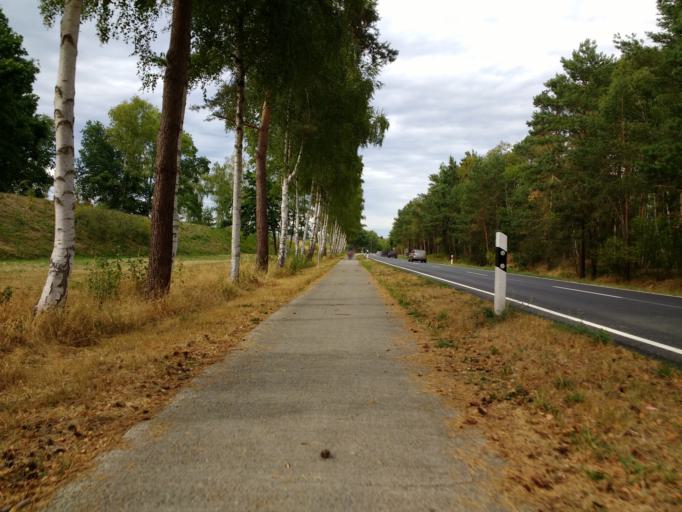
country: DE
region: Lower Saxony
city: Gifhorn
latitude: 52.4646
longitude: 10.5768
